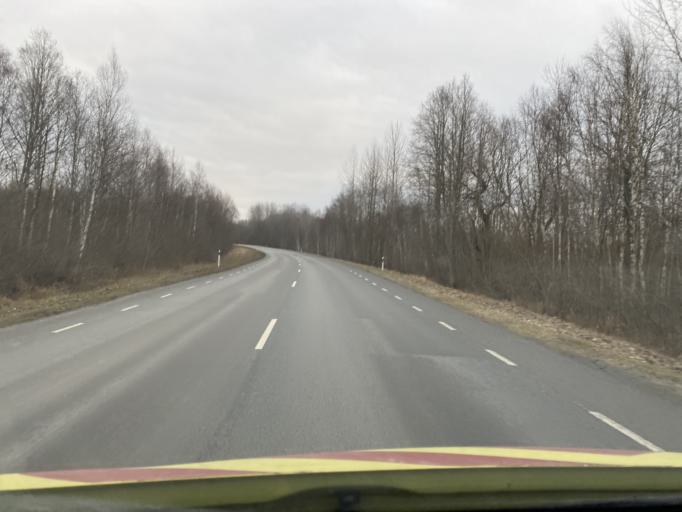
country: EE
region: Laeaene
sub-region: Ridala Parish
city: Uuemoisa
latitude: 58.8339
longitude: 23.6688
